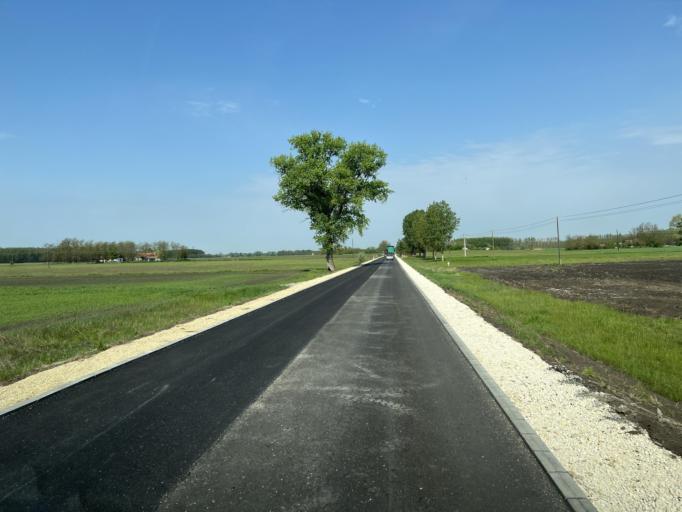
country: HU
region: Pest
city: Kocser
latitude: 46.9874
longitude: 19.9756
